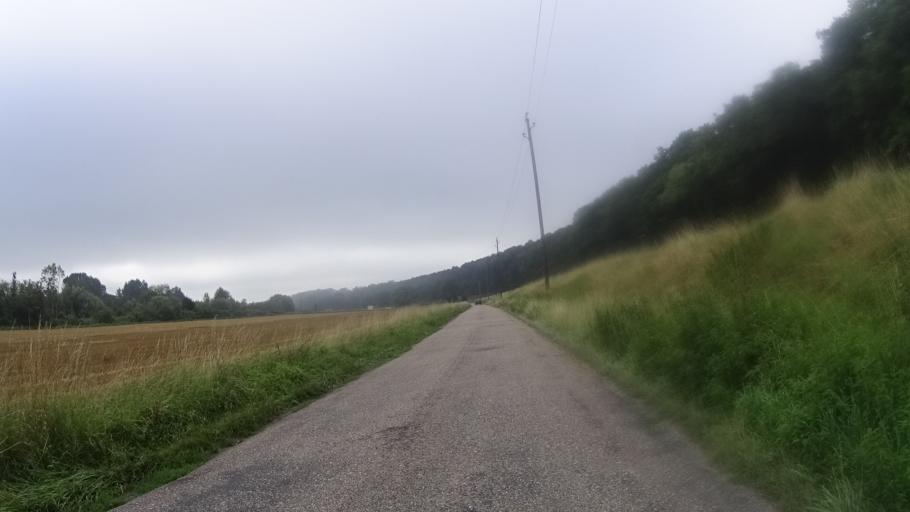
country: FR
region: Lorraine
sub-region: Departement de la Meuse
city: Revigny-sur-Ornain
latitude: 48.8132
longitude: 5.0448
